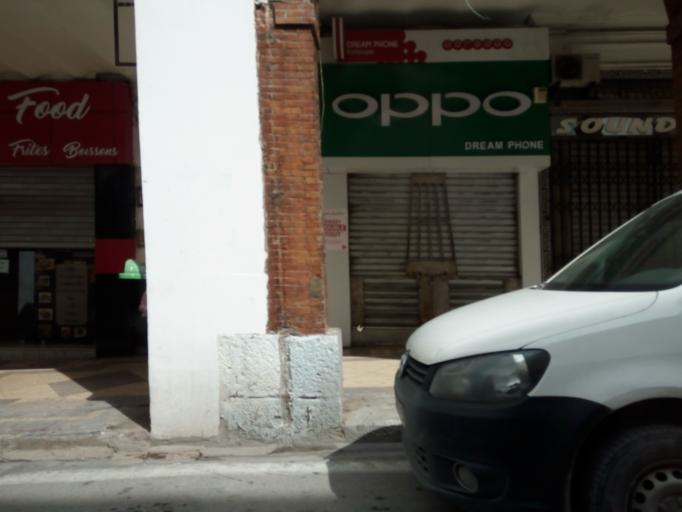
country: DZ
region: Constantine
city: Constantine
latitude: 36.3615
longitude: 6.6075
